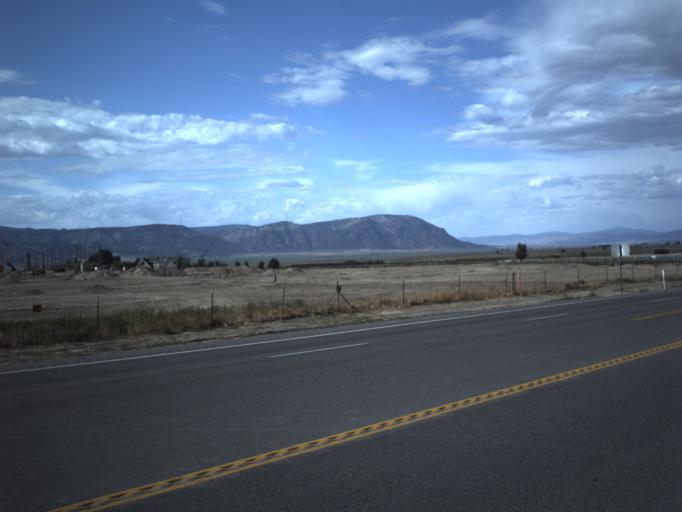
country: US
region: Utah
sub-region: Sanpete County
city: Manti
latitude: 39.2793
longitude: -111.6311
